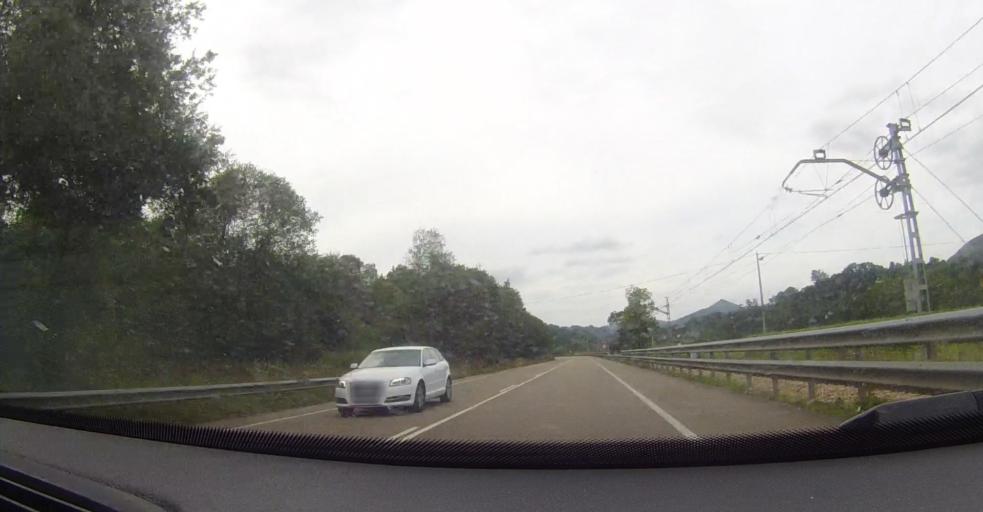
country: ES
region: Asturias
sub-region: Province of Asturias
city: Pilona
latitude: 43.3670
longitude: -5.2843
